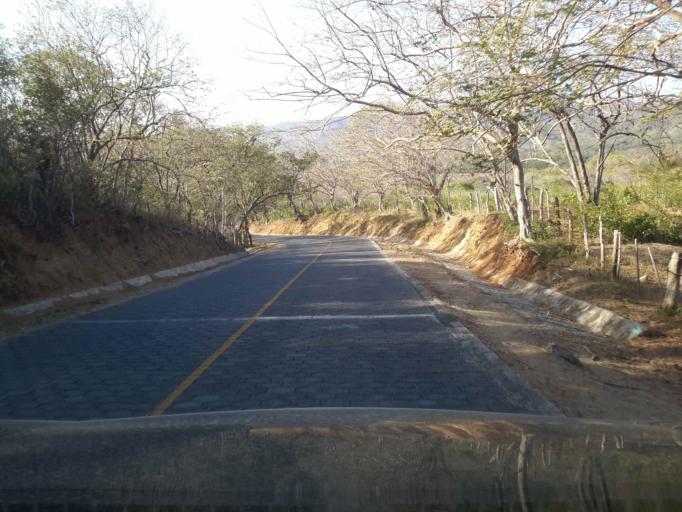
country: NI
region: Rivas
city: San Juan del Sur
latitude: 11.2365
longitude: -85.8316
